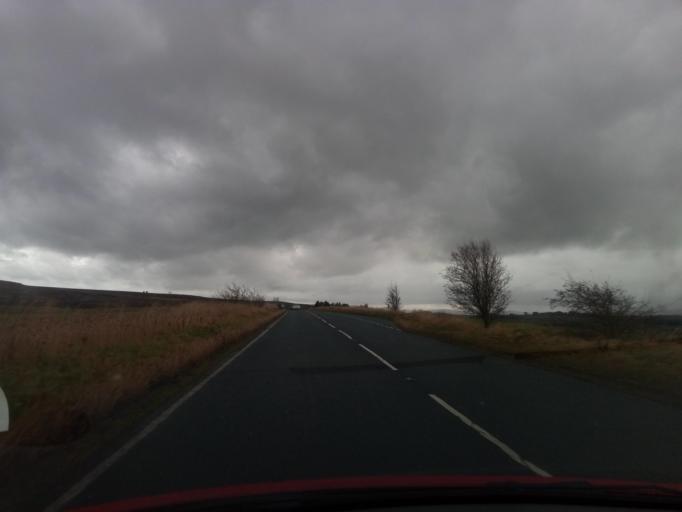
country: GB
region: England
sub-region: Northumberland
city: Rochester
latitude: 55.2555
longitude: -2.2282
